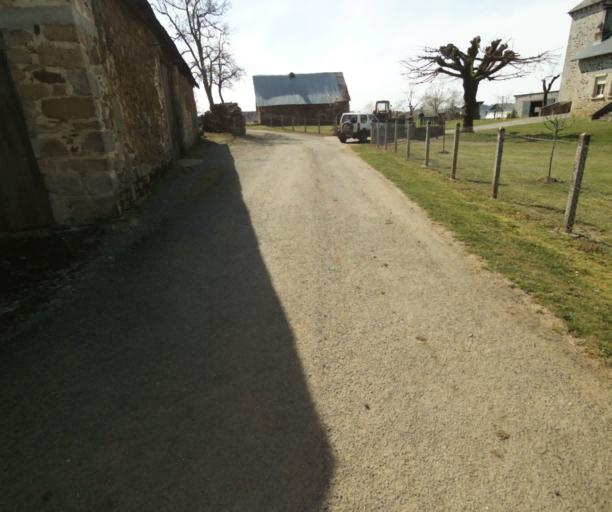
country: FR
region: Limousin
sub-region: Departement de la Correze
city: Naves
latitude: 45.3698
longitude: 1.7760
